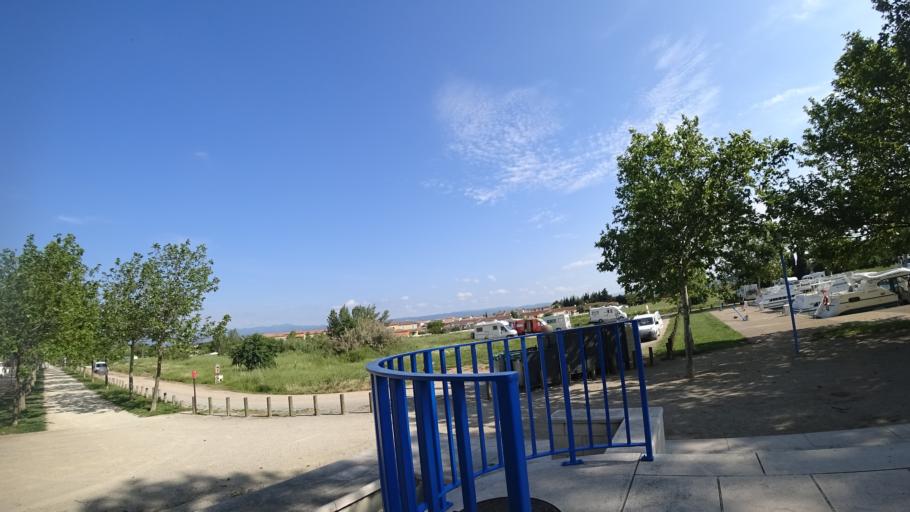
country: FR
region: Languedoc-Roussillon
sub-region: Departement de l'Herault
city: Olonzac
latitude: 43.2684
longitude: 2.7167
